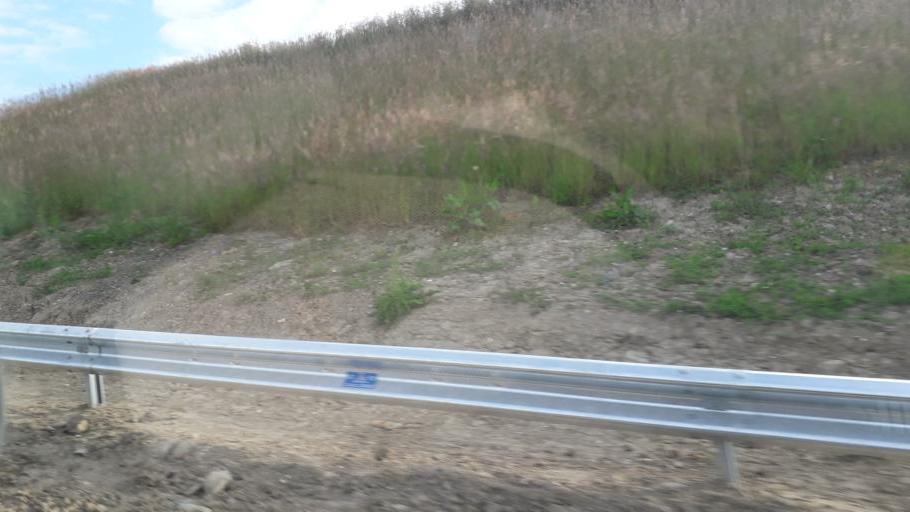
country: IE
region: Leinster
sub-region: Loch Garman
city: Gorey
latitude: 52.6332
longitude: -6.3632
